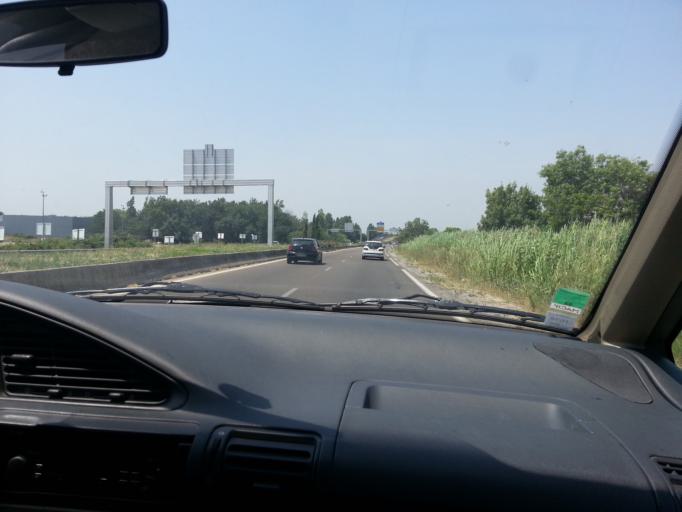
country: FR
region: Languedoc-Roussillon
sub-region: Departement de l'Herault
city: Perols
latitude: 43.5758
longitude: 3.9502
